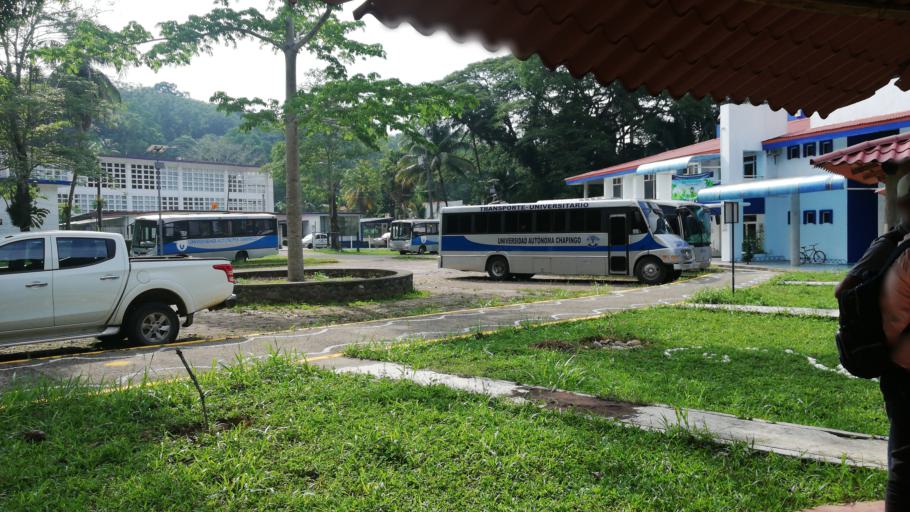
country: MX
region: Tabasco
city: Teapa
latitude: 17.5274
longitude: -92.9303
